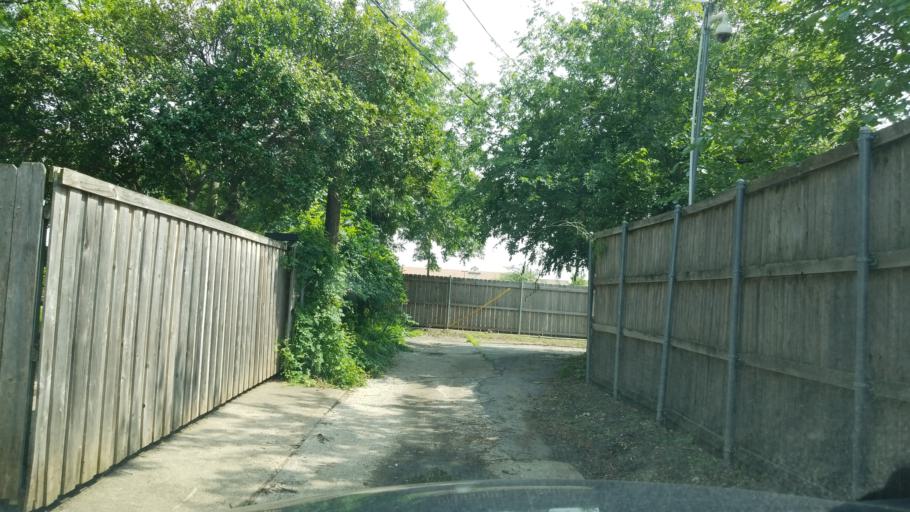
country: US
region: Texas
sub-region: Dallas County
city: Farmers Branch
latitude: 32.8992
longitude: -96.8730
